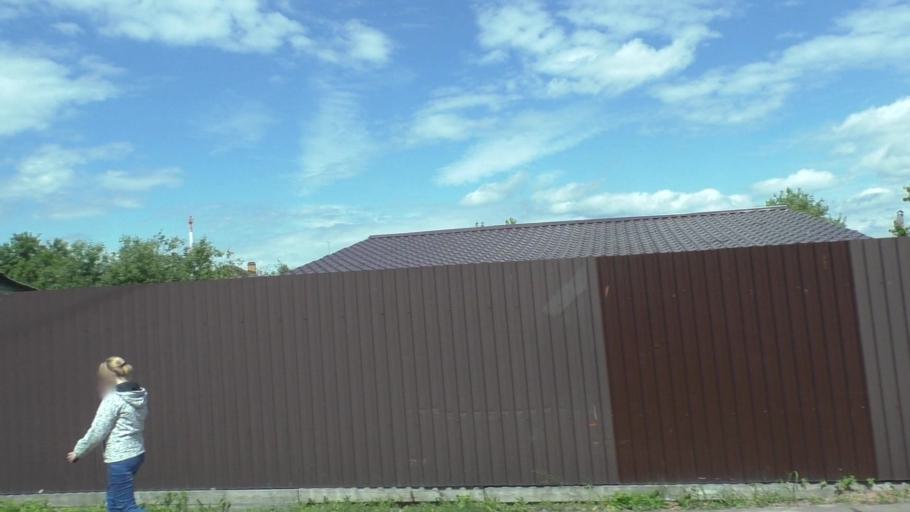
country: RU
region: Moskovskaya
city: Yegor'yevsk
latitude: 55.3825
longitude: 39.0403
